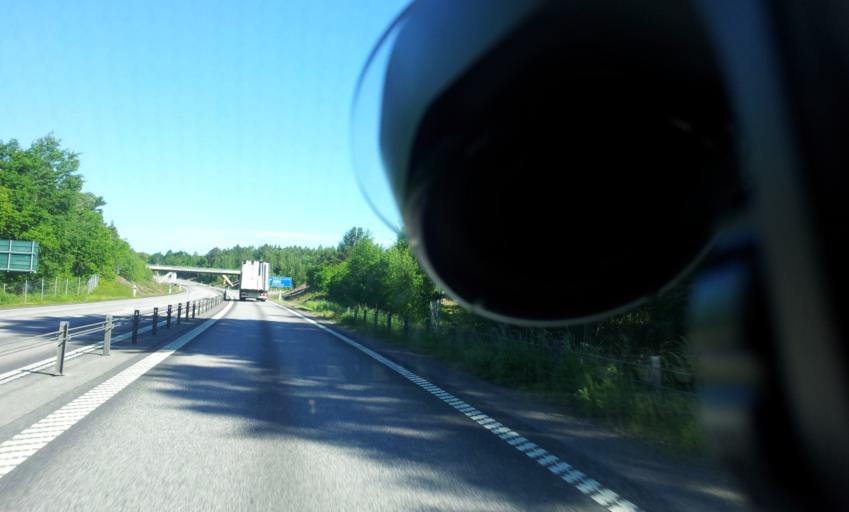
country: SE
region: Kalmar
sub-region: Oskarshamns Kommun
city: Paskallavik
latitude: 57.1490
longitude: 16.4664
